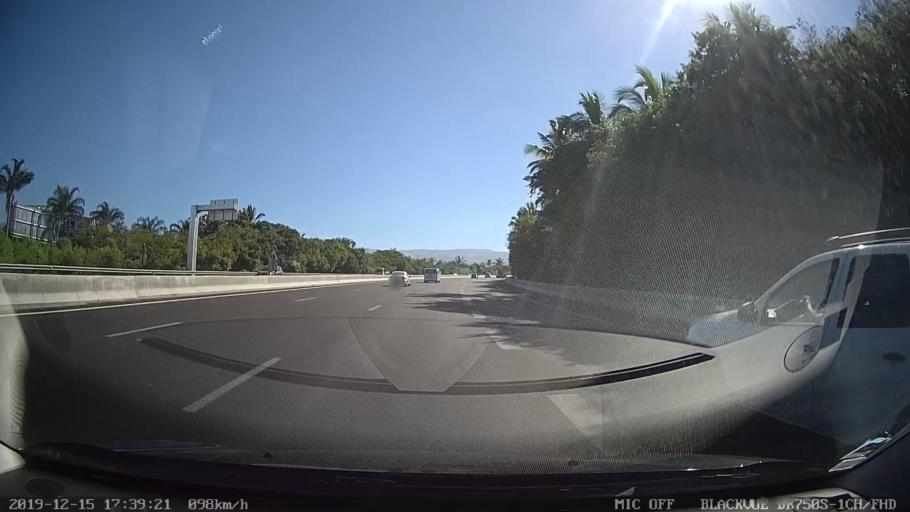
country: RE
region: Reunion
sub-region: Reunion
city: Saint-Pierre
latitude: -21.3233
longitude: 55.4765
